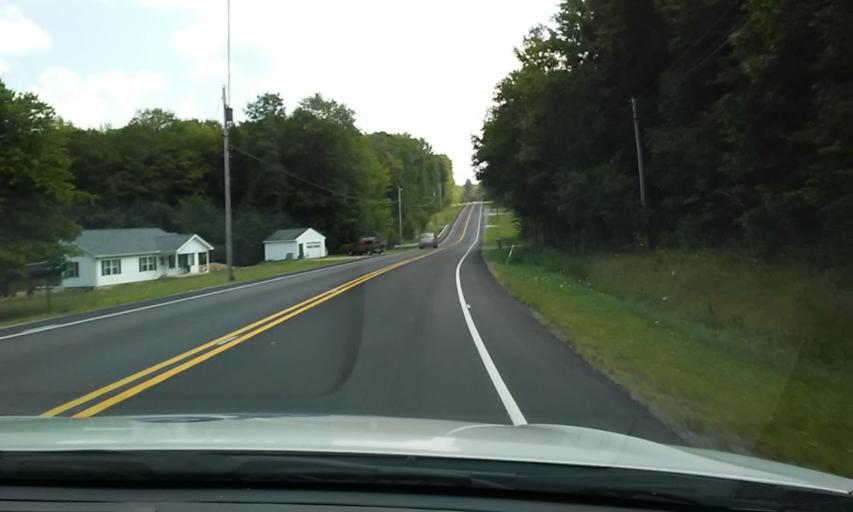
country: US
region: Pennsylvania
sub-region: Elk County
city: Saint Marys
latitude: 41.4448
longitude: -78.4962
